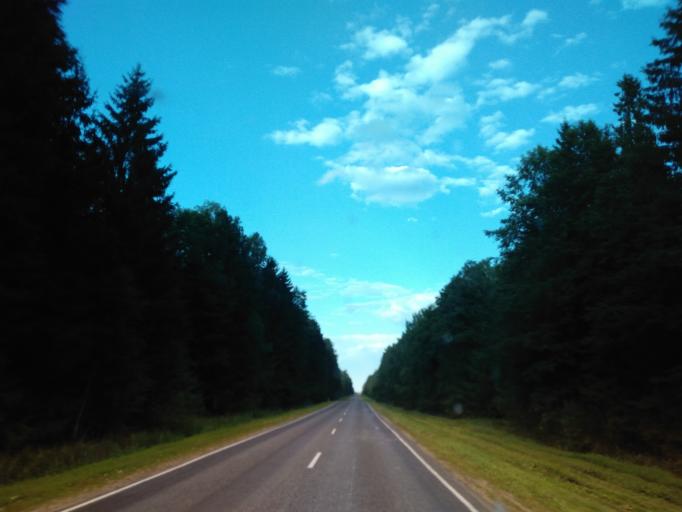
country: BY
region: Minsk
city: Uzda
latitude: 53.4295
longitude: 27.4597
